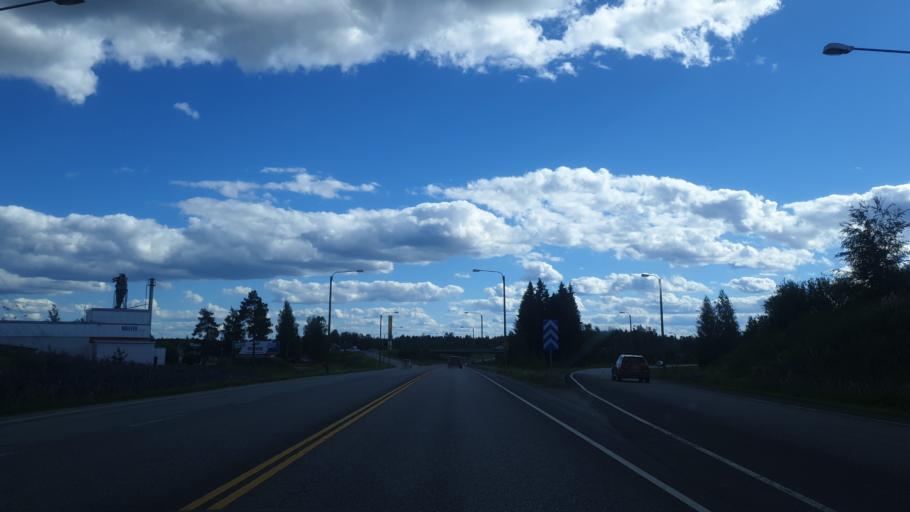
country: FI
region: Southern Savonia
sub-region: Pieksaemaeki
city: Juva
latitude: 61.9024
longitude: 27.8041
